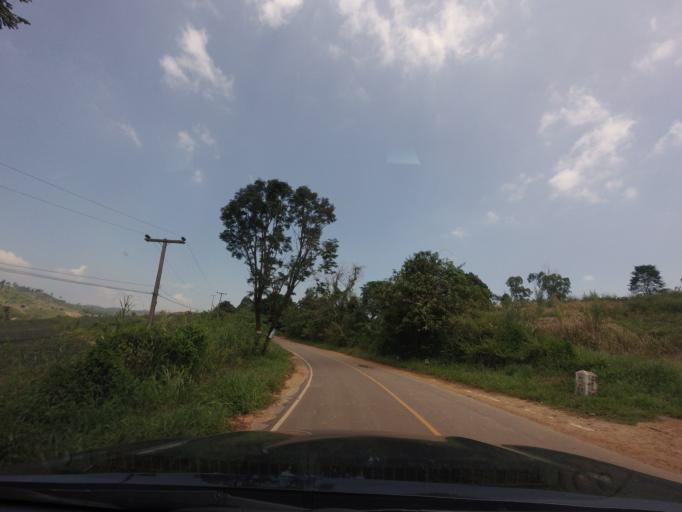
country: TH
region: Loei
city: Na Haeo
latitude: 17.5269
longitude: 100.8799
